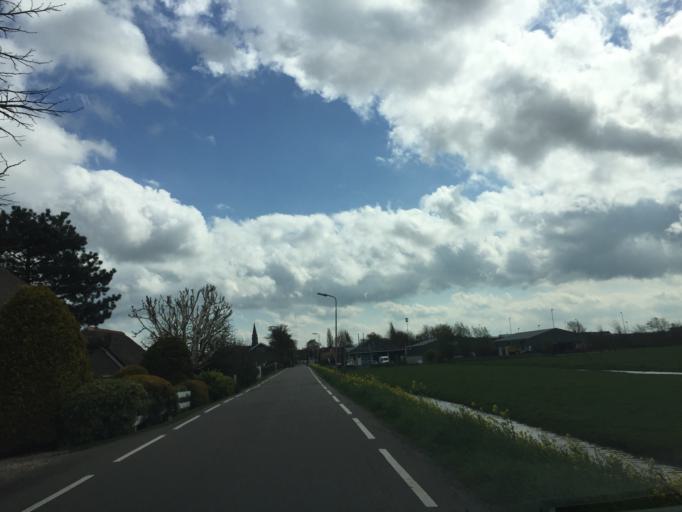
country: NL
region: South Holland
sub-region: Gemeente Gouda
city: Bloemendaal
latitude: 52.0567
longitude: 4.6838
